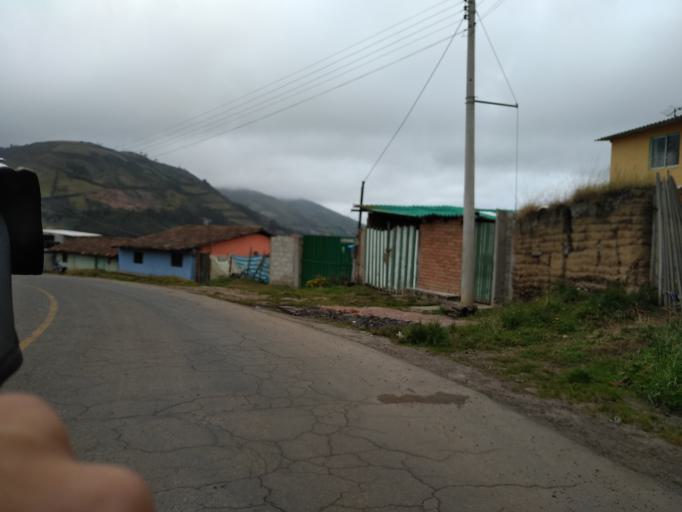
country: EC
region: Carchi
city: El Angel
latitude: 0.6339
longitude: -77.9345
